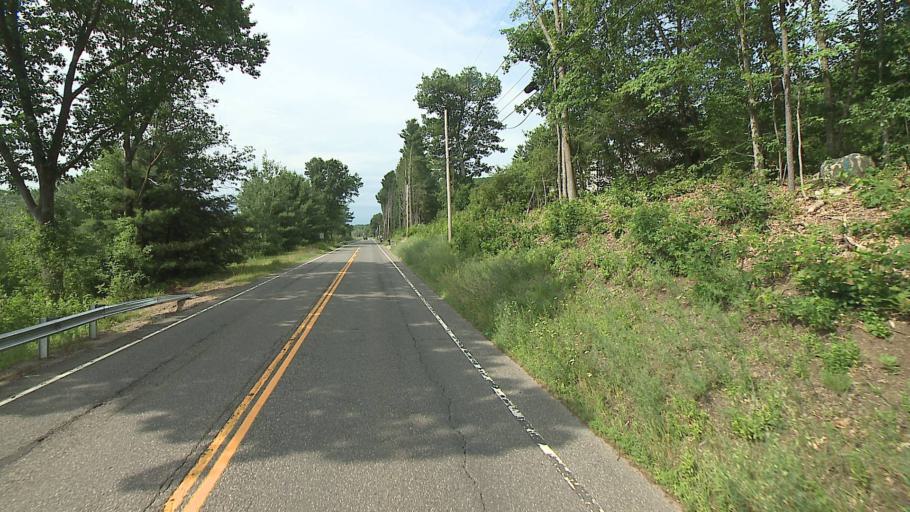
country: US
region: Connecticut
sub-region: Litchfield County
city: Winchester Center
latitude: 41.8614
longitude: -73.0893
